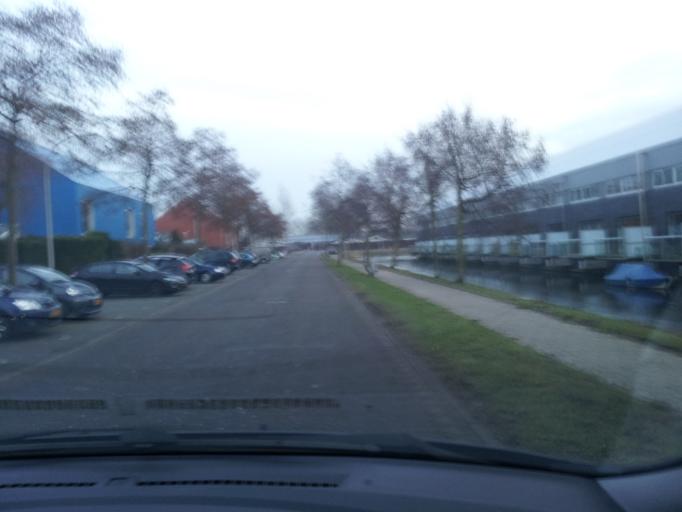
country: NL
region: South Holland
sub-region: Gemeente Den Haag
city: Ypenburg
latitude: 52.0347
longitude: 4.3689
